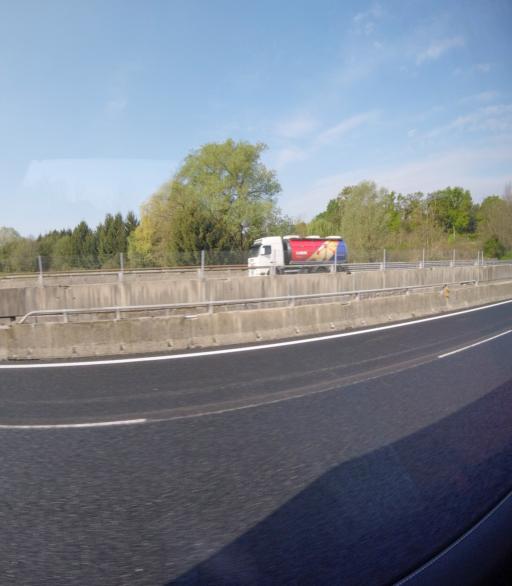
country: IT
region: Piedmont
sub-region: Provincia di Novara
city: Borgo Ticino
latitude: 45.7026
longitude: 8.6052
